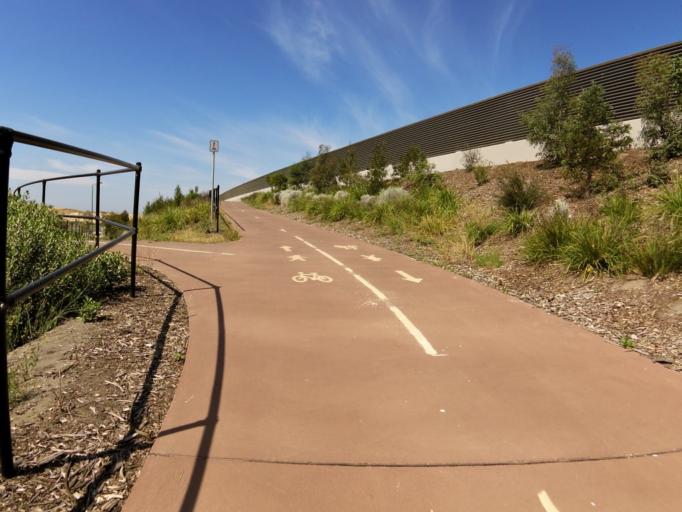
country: AU
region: Victoria
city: Heatherton
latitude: -37.9479
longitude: 145.1002
